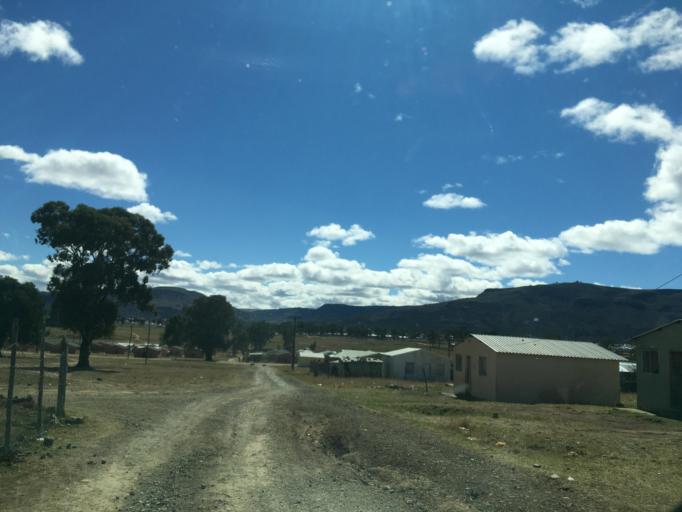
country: ZA
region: Eastern Cape
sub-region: Chris Hani District Municipality
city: Cala
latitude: -31.5424
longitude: 27.6834
